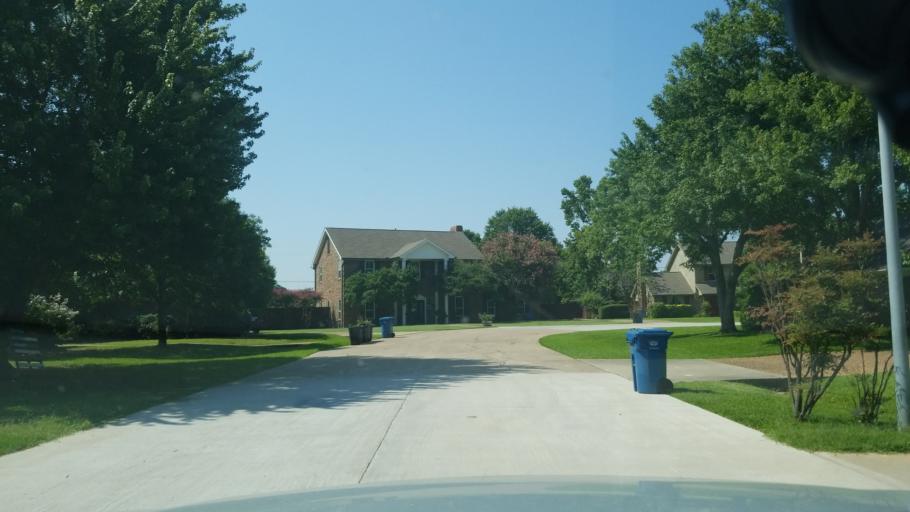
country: US
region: Texas
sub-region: Dallas County
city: Coppell
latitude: 32.9665
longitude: -96.9983
